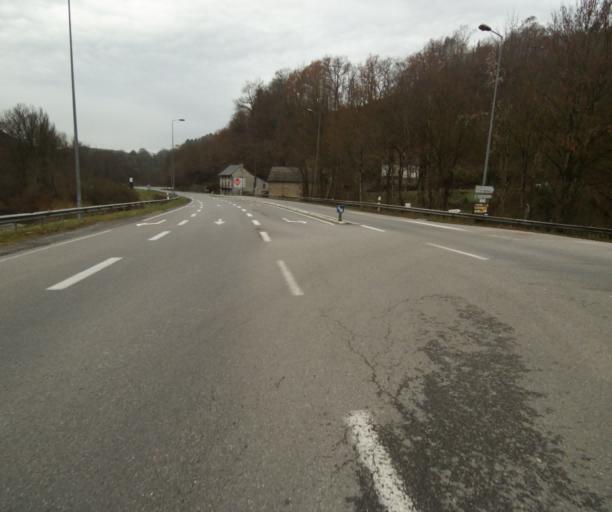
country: FR
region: Limousin
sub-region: Departement de la Correze
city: Chameyrat
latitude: 45.2393
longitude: 1.7352
